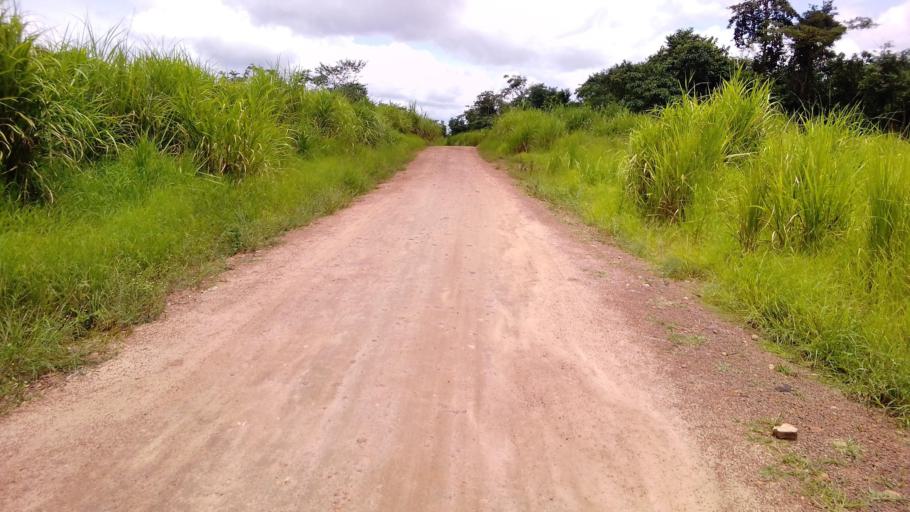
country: SL
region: Eastern Province
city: Koidu
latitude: 8.6842
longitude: -10.9329
